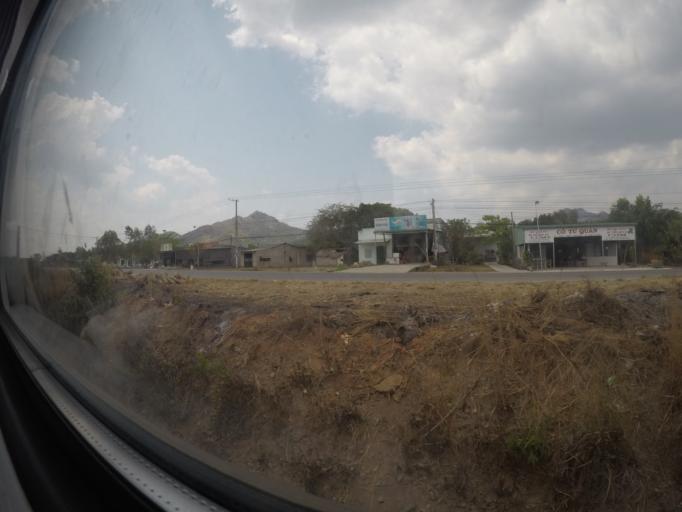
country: VN
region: Binh Thuan
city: Tanh Linh
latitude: 10.9639
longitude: 107.6379
